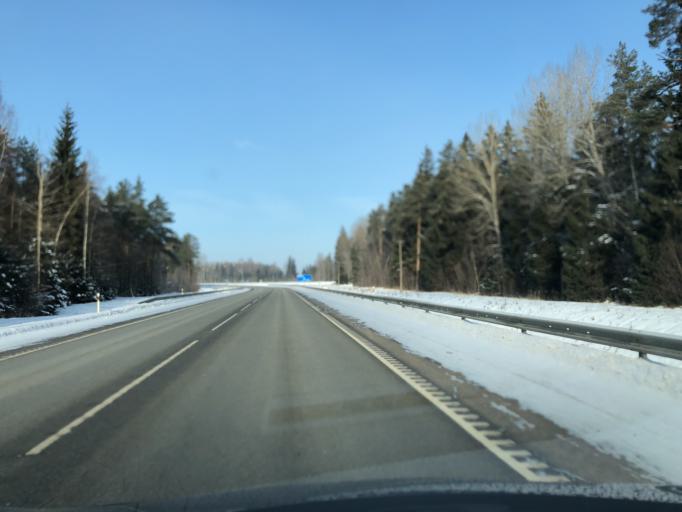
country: EE
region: Tartu
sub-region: Tartu linn
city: Tartu
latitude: 58.4053
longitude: 26.6538
